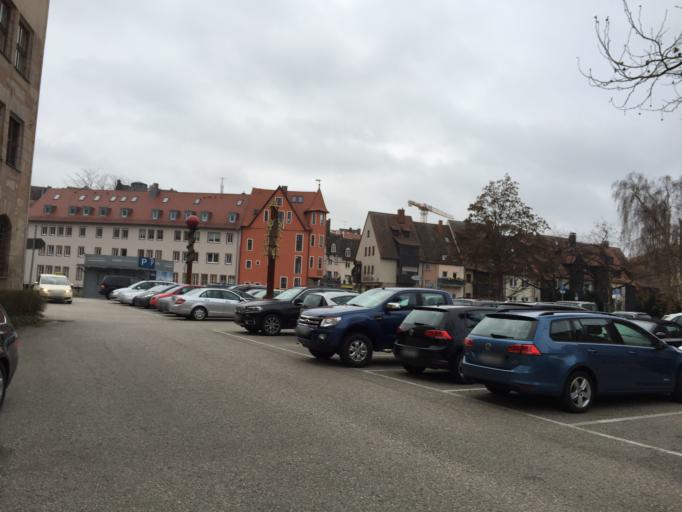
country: DE
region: Bavaria
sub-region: Regierungsbezirk Mittelfranken
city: Nuernberg
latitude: 49.4541
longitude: 11.0749
